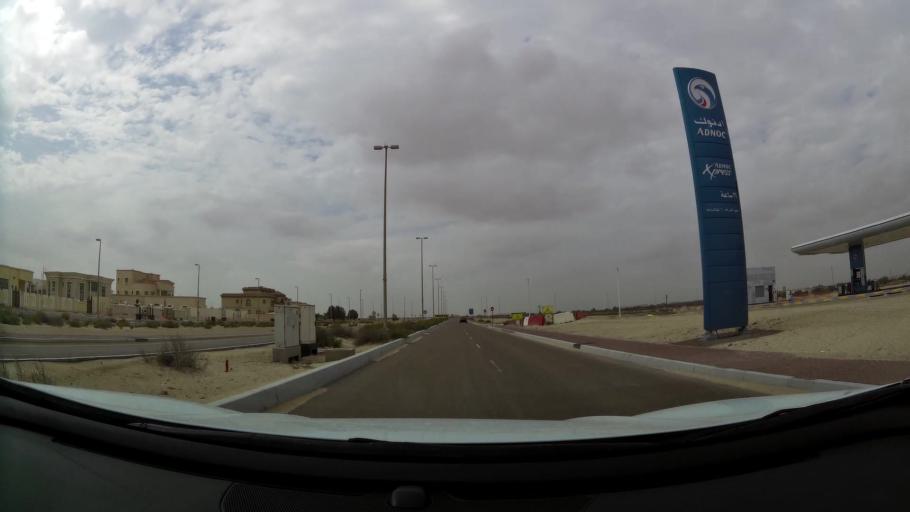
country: AE
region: Abu Dhabi
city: Abu Dhabi
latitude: 24.4014
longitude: 54.6546
